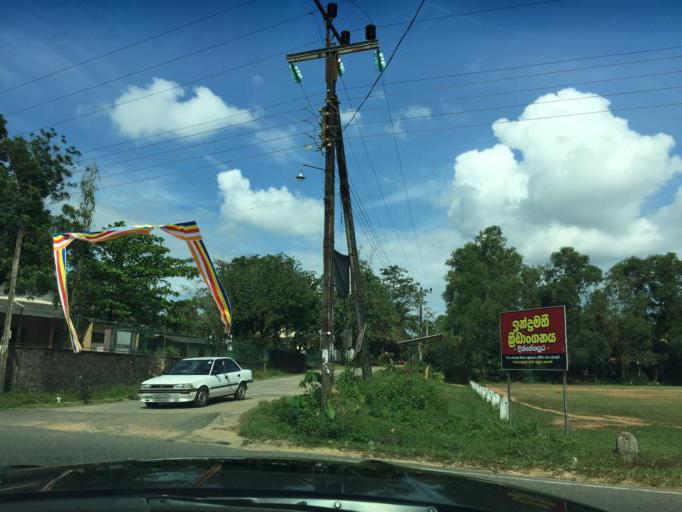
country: LK
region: Western
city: Horana South
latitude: 6.7149
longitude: 80.0801
